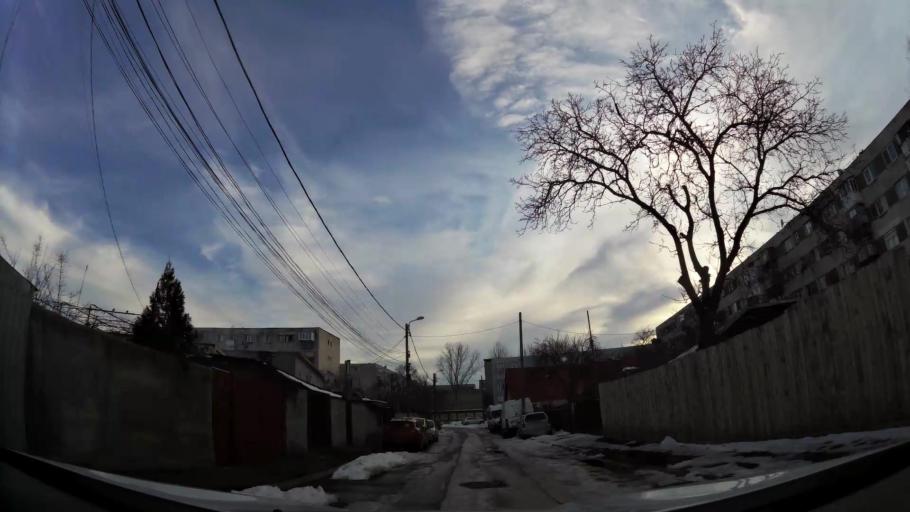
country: RO
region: Bucuresti
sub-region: Municipiul Bucuresti
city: Bucuresti
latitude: 44.3917
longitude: 26.0744
